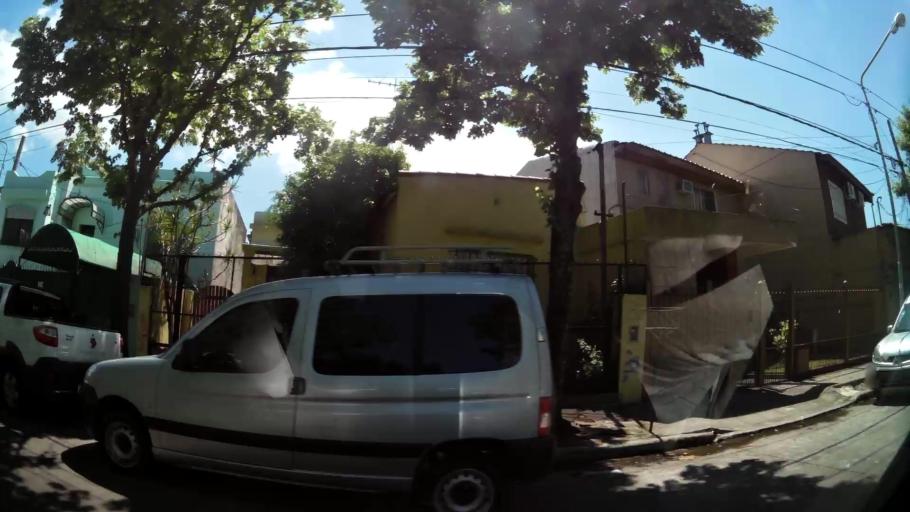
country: AR
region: Buenos Aires
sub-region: Partido de Tigre
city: Tigre
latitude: -34.4301
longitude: -58.5734
